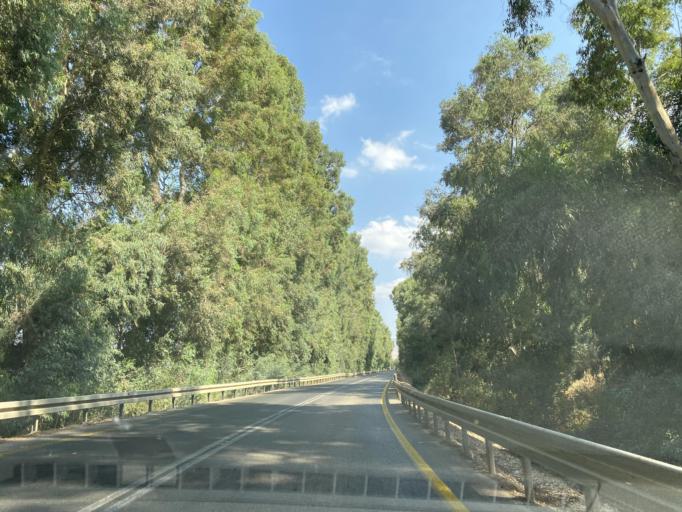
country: IL
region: Northern District
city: Qiryat Shemona
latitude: 33.1684
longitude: 35.5840
